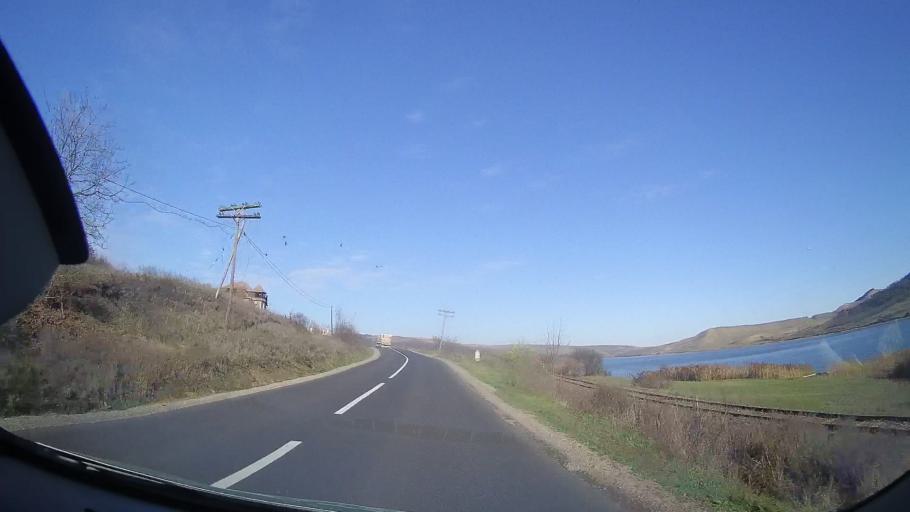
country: RO
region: Mures
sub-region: Comuna Zau De Campie
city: Zau de Campie
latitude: 46.6255
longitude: 24.1328
